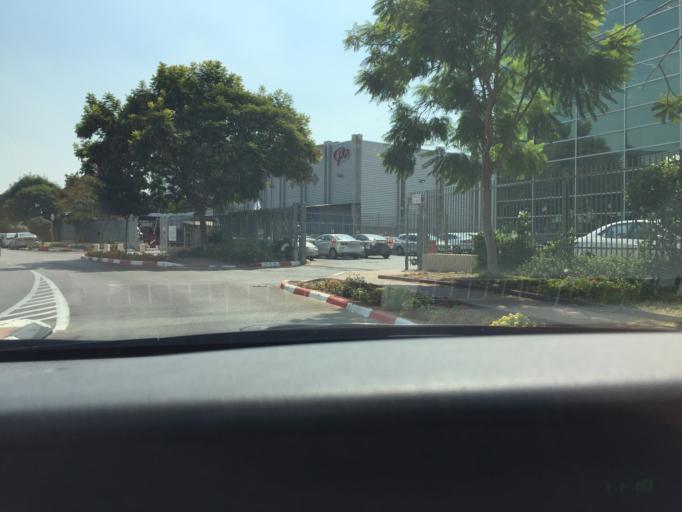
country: IL
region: Central District
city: Yehud
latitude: 31.9908
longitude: 34.9100
